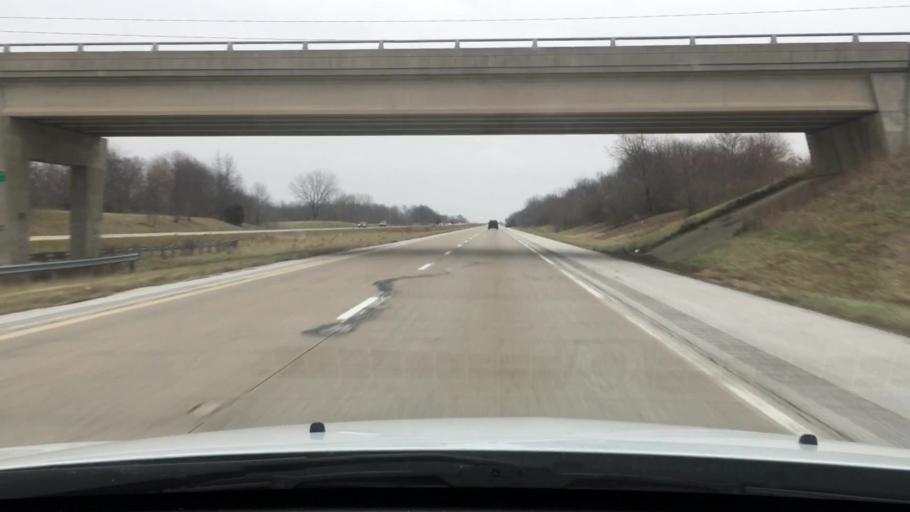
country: US
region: Illinois
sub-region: Scott County
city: Winchester
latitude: 39.6810
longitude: -90.5037
